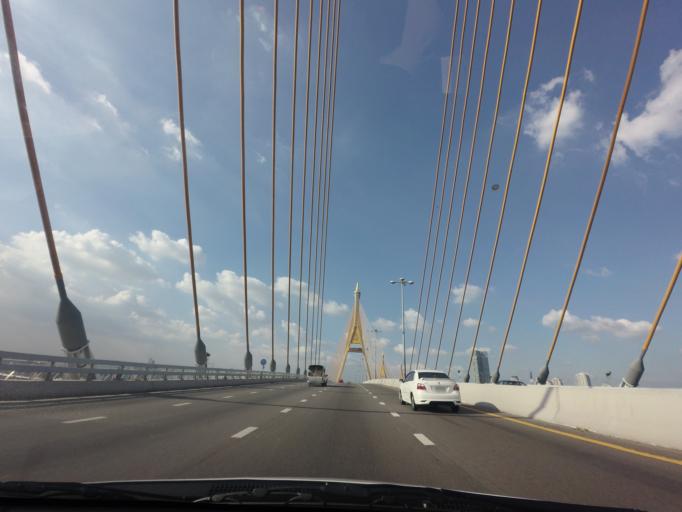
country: TH
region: Samut Prakan
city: Phra Pradaeng
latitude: 13.6594
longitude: 100.5395
